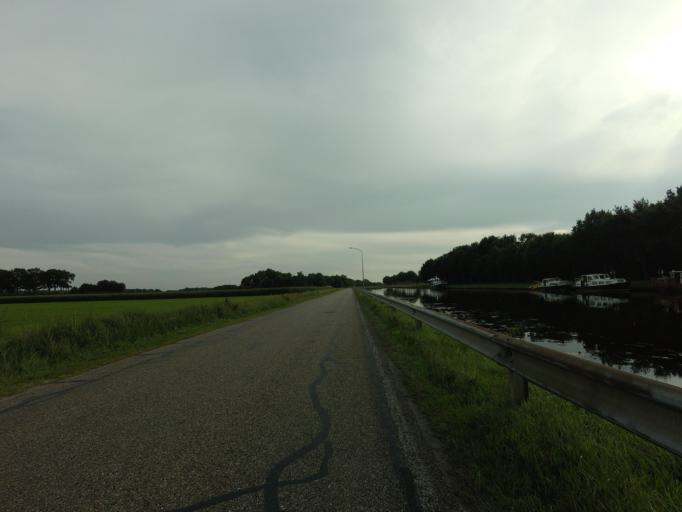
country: DE
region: Lower Saxony
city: Laar
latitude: 52.6059
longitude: 6.6763
